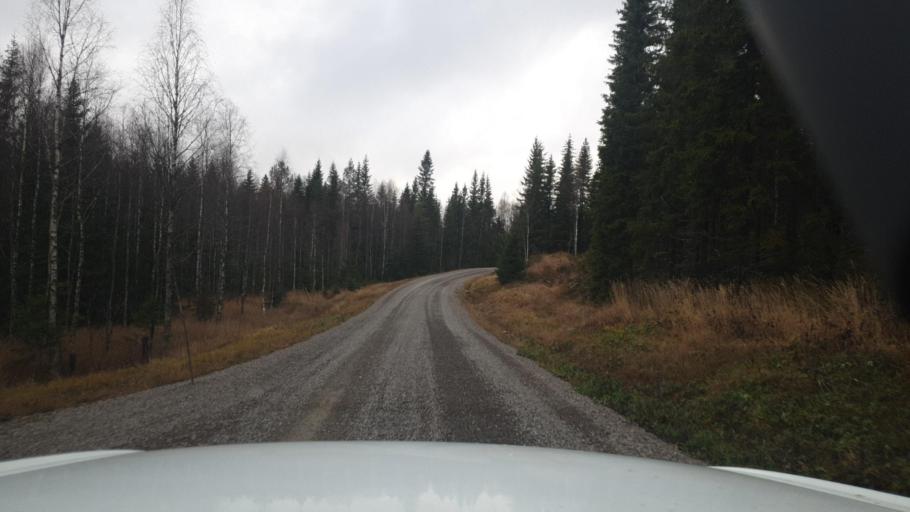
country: SE
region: Vaermland
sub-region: Eda Kommun
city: Charlottenberg
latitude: 60.0964
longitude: 12.6111
